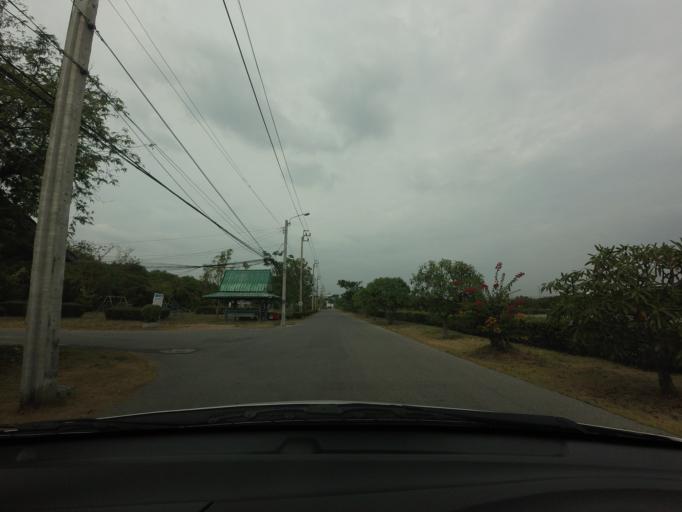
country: TH
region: Samut Prakan
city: Samut Prakan
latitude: 13.5207
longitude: 100.6480
